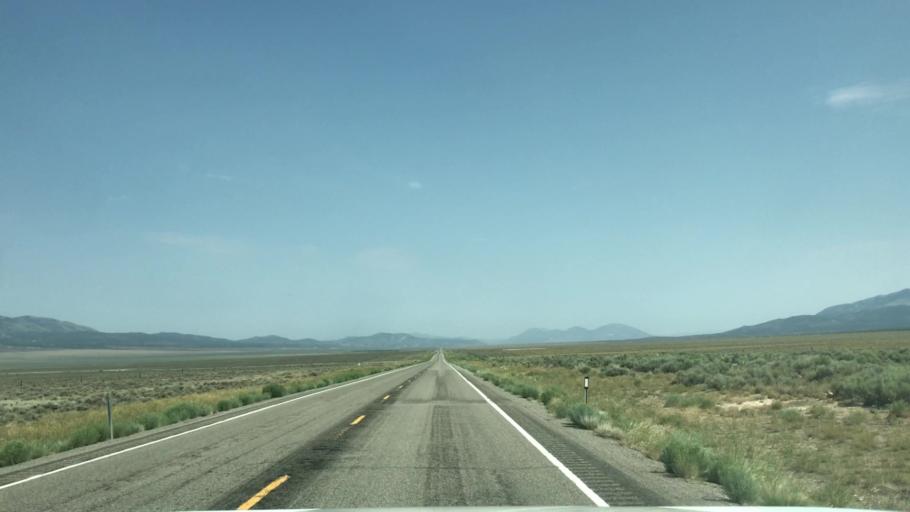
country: US
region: Nevada
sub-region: White Pine County
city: Ely
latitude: 39.0617
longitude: -114.7328
